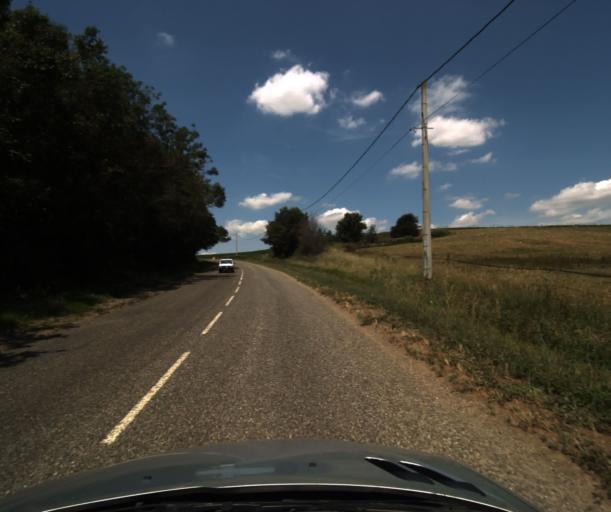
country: FR
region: Midi-Pyrenees
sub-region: Departement de la Haute-Garonne
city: Saint-Lys
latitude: 43.4919
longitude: 1.2098
